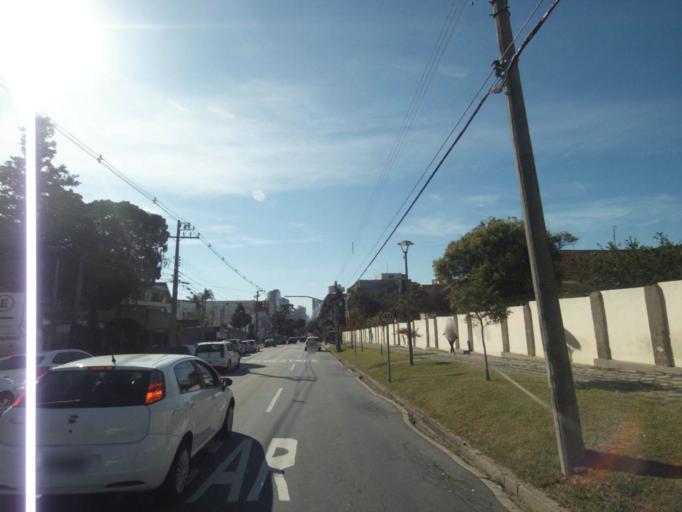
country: BR
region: Parana
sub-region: Curitiba
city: Curitiba
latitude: -25.4387
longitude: -49.2907
